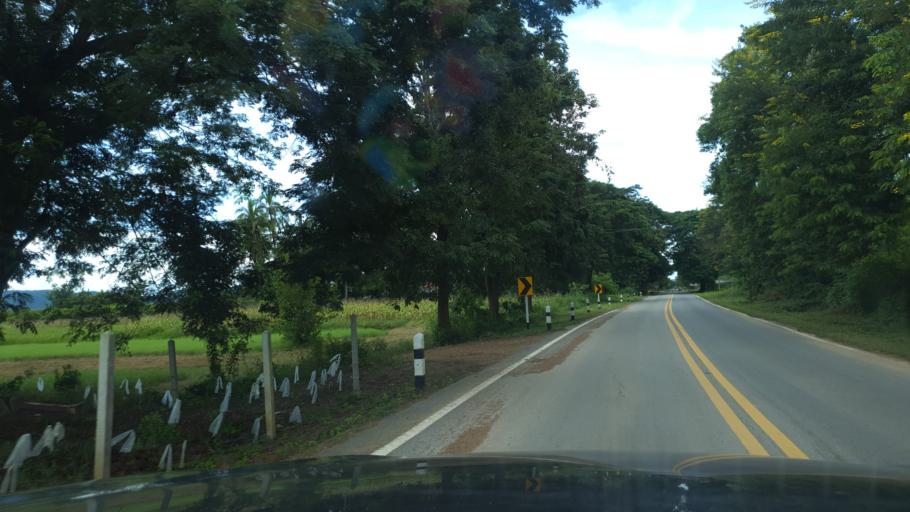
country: TH
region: Sukhothai
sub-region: Amphoe Si Satchanalai
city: Si Satchanalai
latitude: 17.4763
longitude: 99.7539
